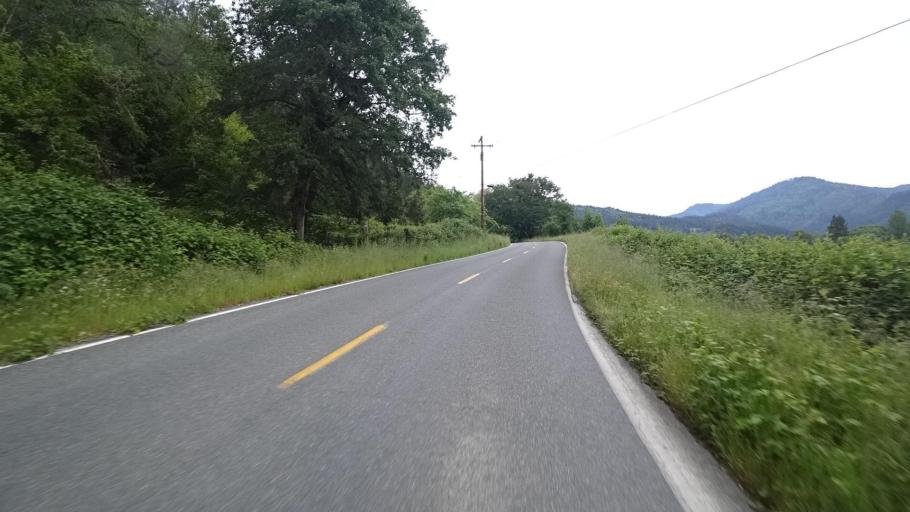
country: US
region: California
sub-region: Humboldt County
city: Willow Creek
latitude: 41.0905
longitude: -123.7132
